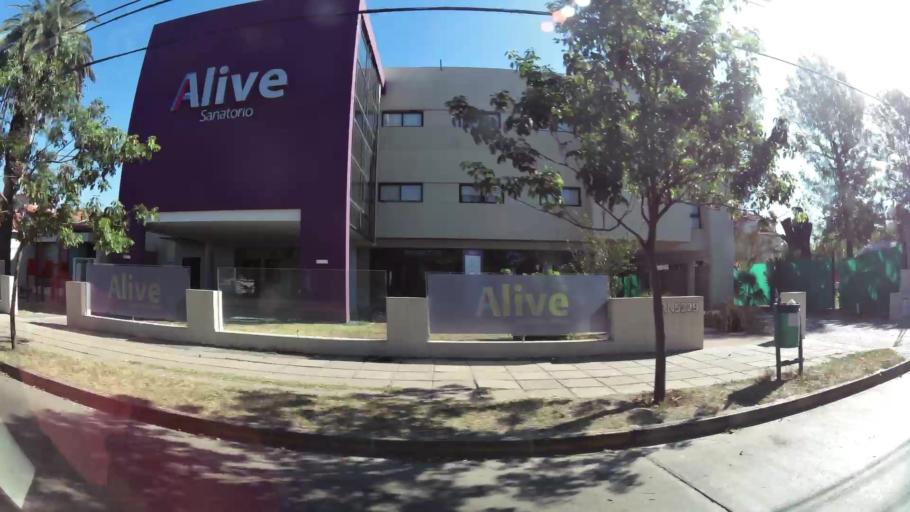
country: AR
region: Cordoba
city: Villa Allende
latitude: -31.3557
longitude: -64.2431
